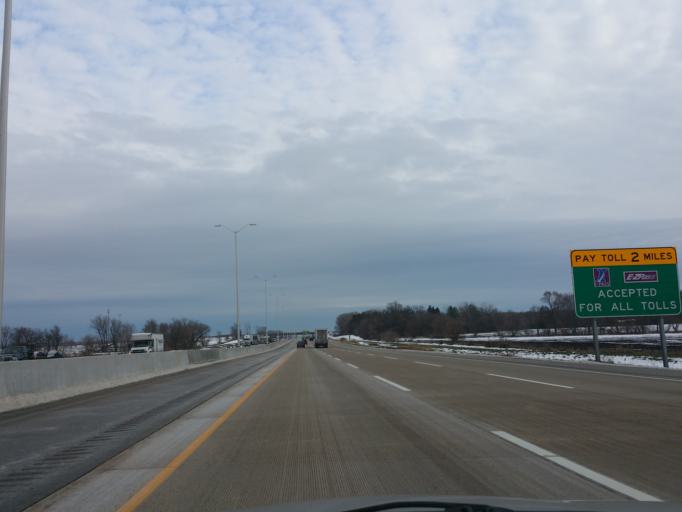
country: US
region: Illinois
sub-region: McHenry County
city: Marengo
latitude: 42.1809
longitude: -88.6274
